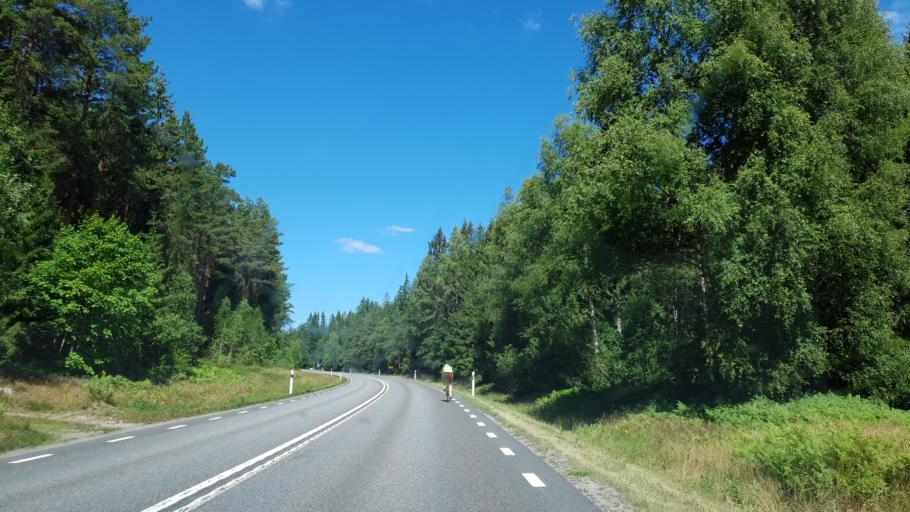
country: SE
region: Joenkoeping
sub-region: Varnamo Kommun
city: Rydaholm
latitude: 56.9232
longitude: 14.4180
